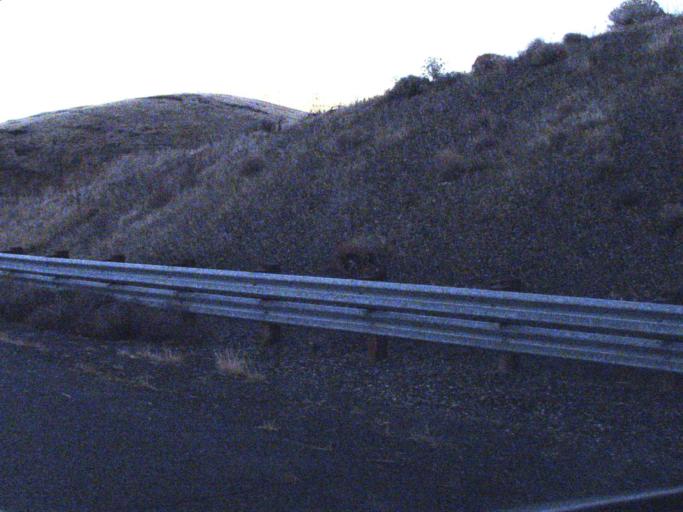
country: US
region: Washington
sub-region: Garfield County
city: Pomeroy
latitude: 46.6125
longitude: -117.7903
